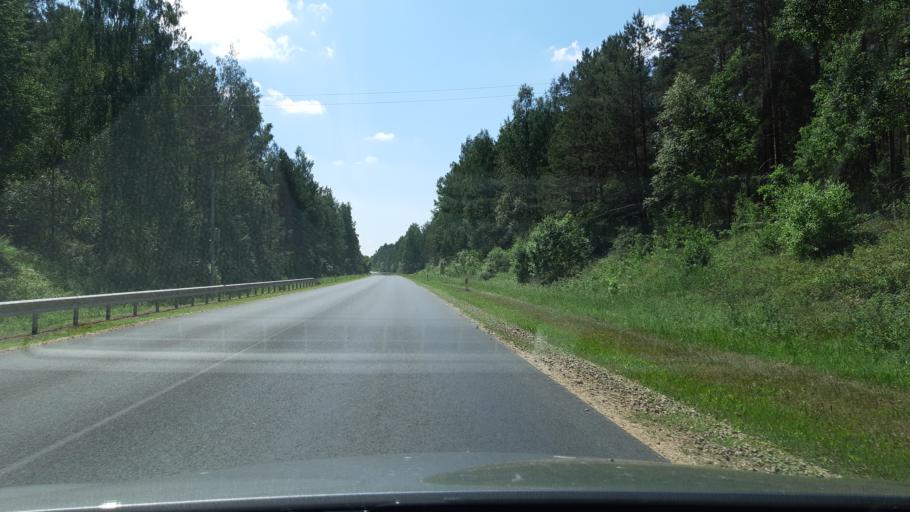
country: LT
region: Alytaus apskritis
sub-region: Alytaus rajonas
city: Daugai
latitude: 54.1602
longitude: 24.2086
